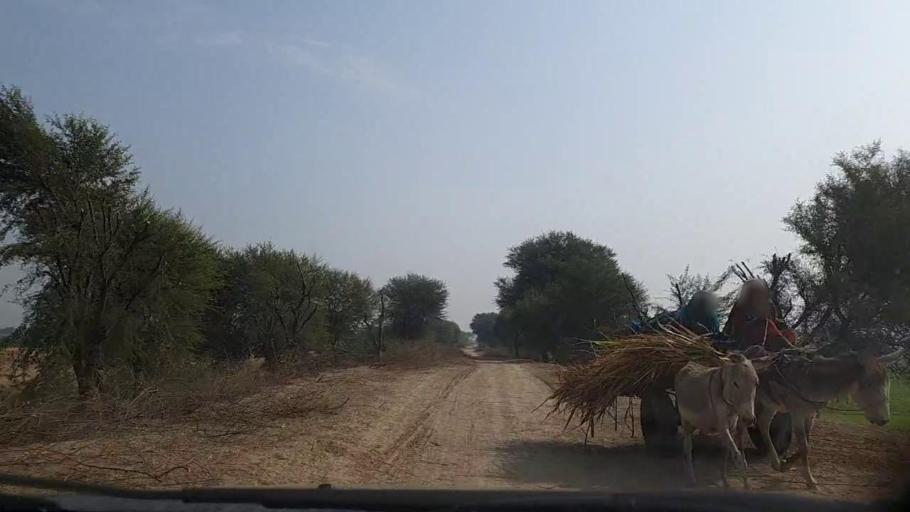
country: PK
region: Sindh
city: Sanghar
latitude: 26.0514
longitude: 68.9801
